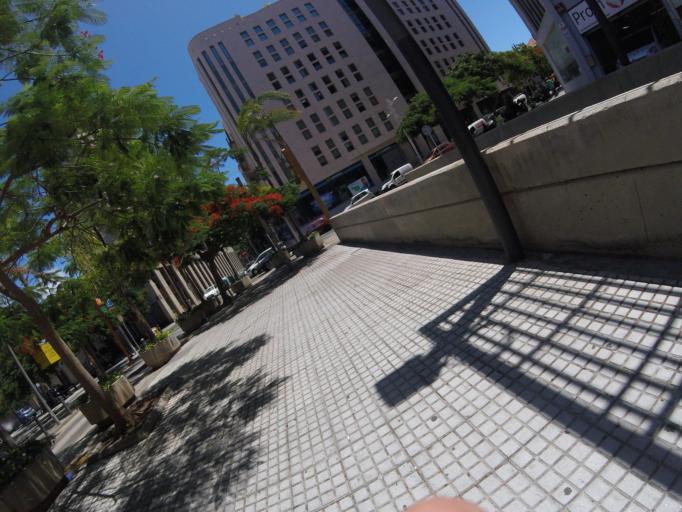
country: ES
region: Canary Islands
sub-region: Provincia de Santa Cruz de Tenerife
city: Santa Cruz de Tenerife
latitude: 28.4700
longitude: -16.2517
